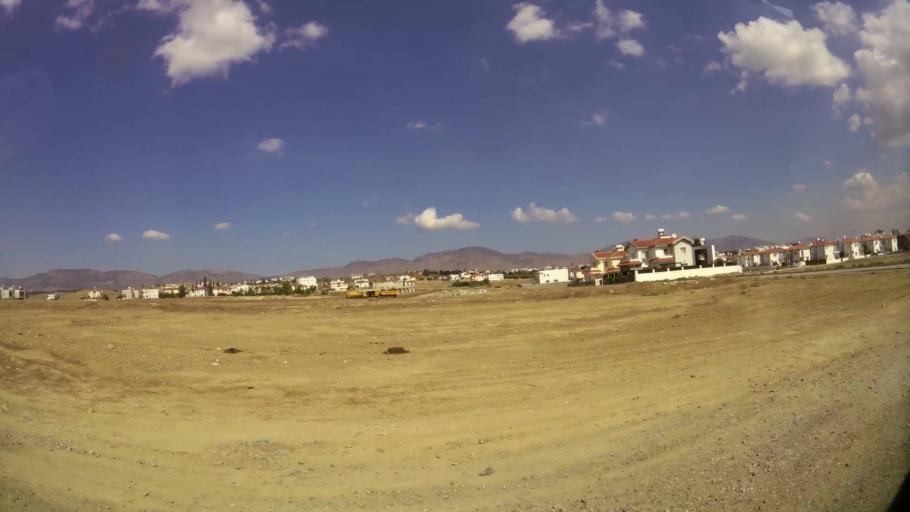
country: CY
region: Lefkosia
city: Nicosia
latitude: 35.2216
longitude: 33.2917
